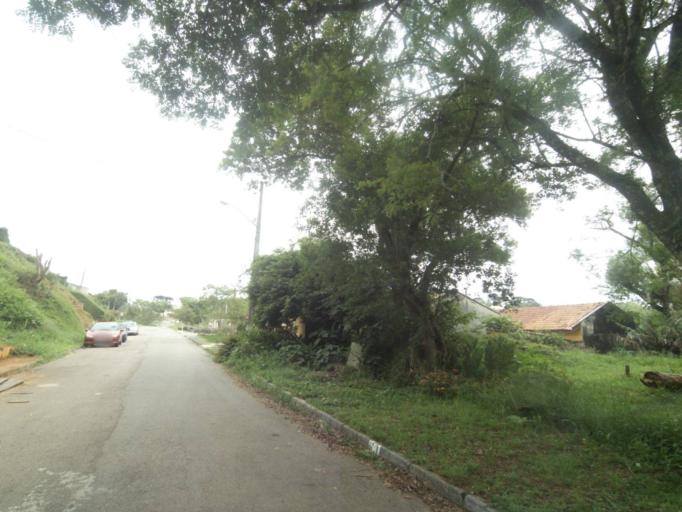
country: BR
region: Parana
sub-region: Curitiba
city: Curitiba
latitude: -25.3924
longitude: -49.2785
